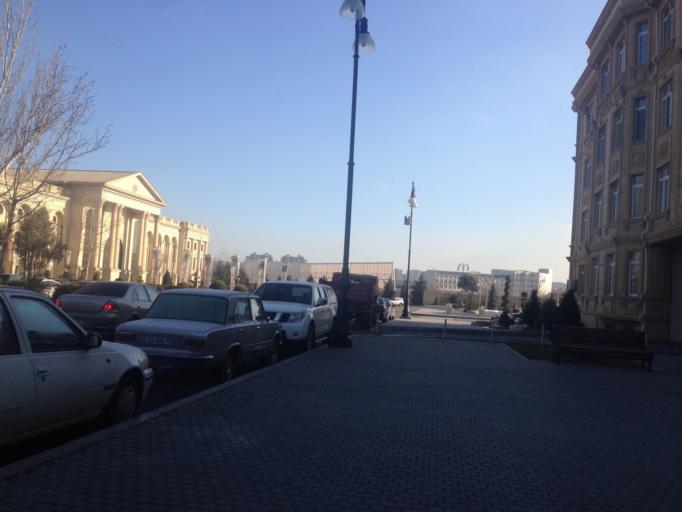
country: AZ
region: Baki
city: Baku
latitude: 40.4053
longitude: 49.8551
